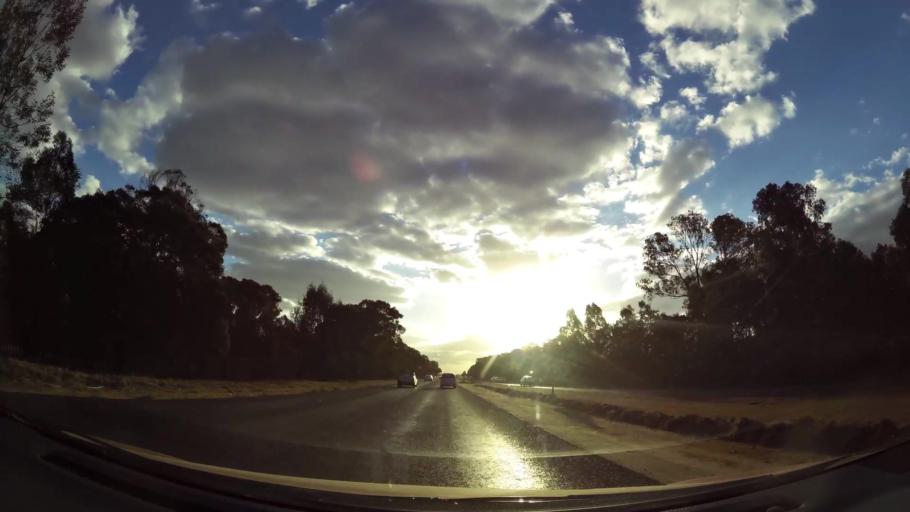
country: ZA
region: Gauteng
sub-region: City of Johannesburg Metropolitan Municipality
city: Midrand
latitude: -25.9451
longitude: 28.1499
